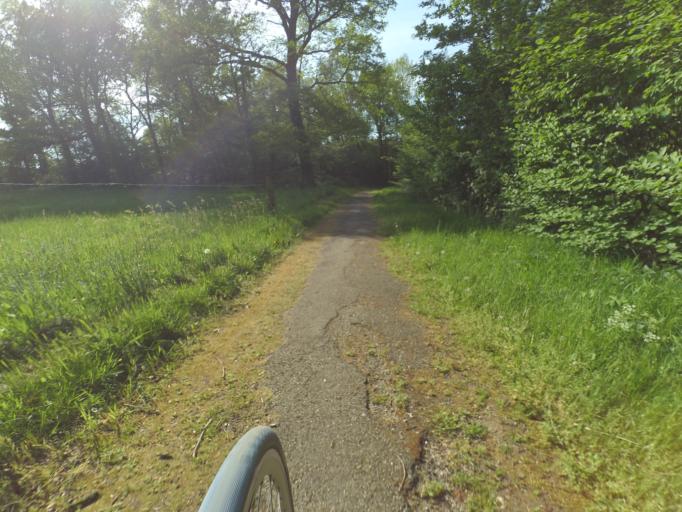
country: NL
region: Overijssel
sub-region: Gemeente Oldenzaal
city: Oldenzaal
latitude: 52.3830
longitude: 6.9488
